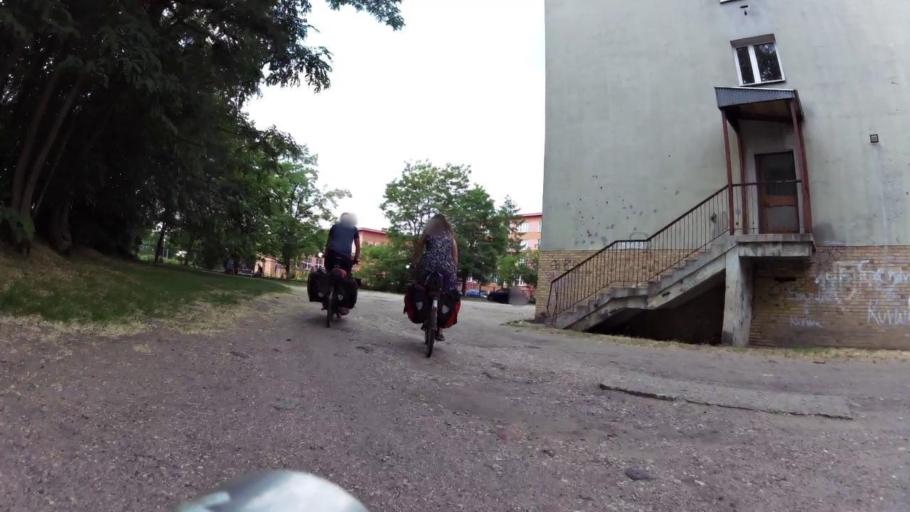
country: PL
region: Kujawsko-Pomorskie
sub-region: Bydgoszcz
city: Fordon
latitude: 53.1442
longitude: 18.1597
